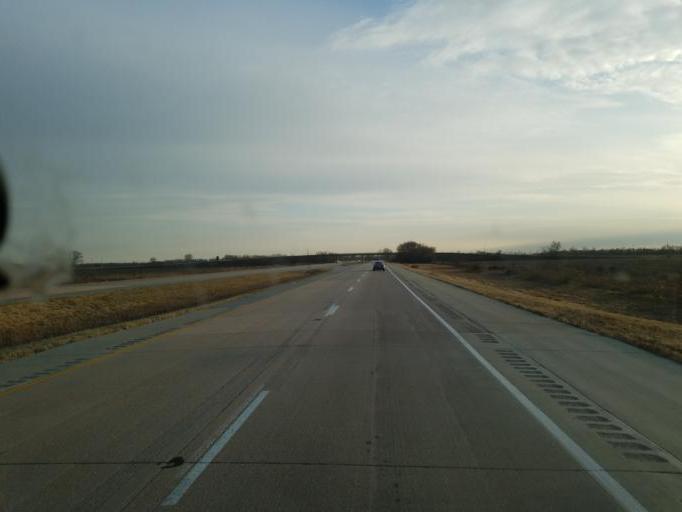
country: US
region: Nebraska
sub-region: Burt County
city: Tekamah
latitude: 41.8613
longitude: -96.1028
